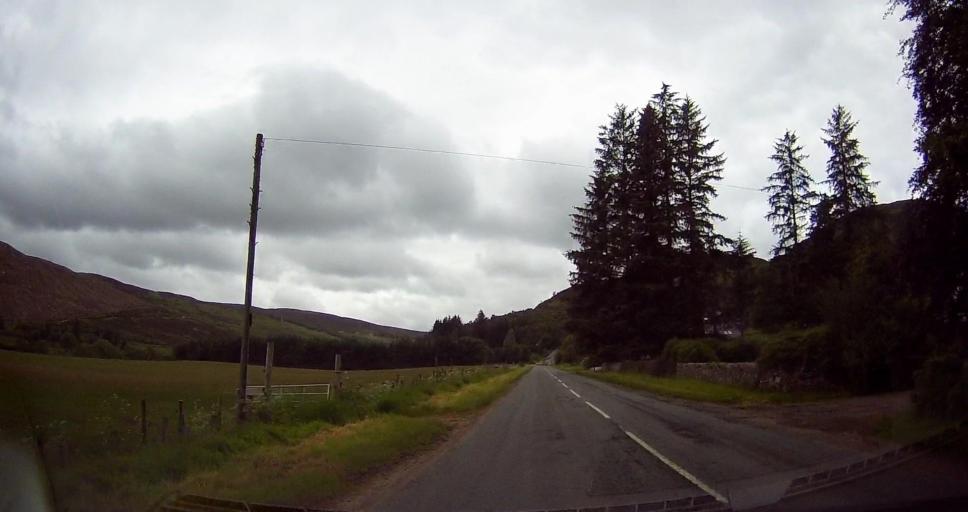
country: GB
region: Scotland
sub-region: Highland
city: Dornoch
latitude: 58.0051
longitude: -4.1789
